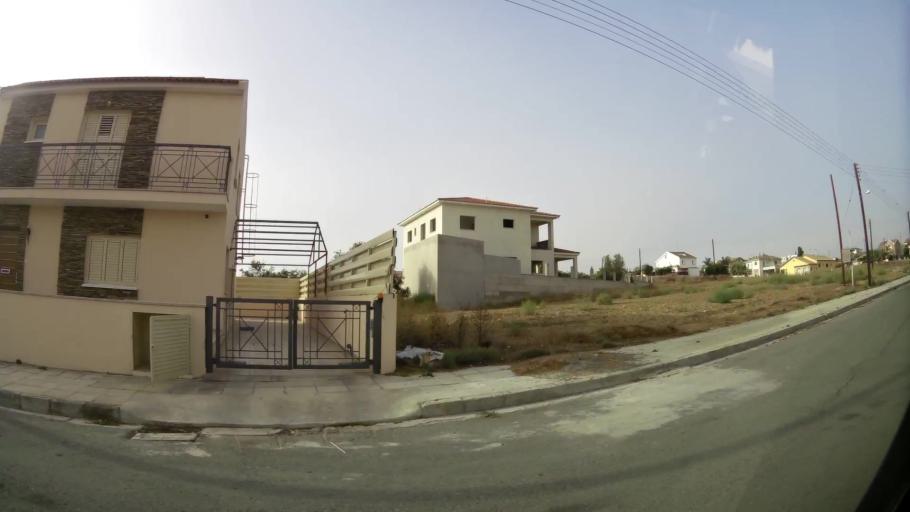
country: CY
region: Lefkosia
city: Geri
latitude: 35.0688
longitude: 33.3939
